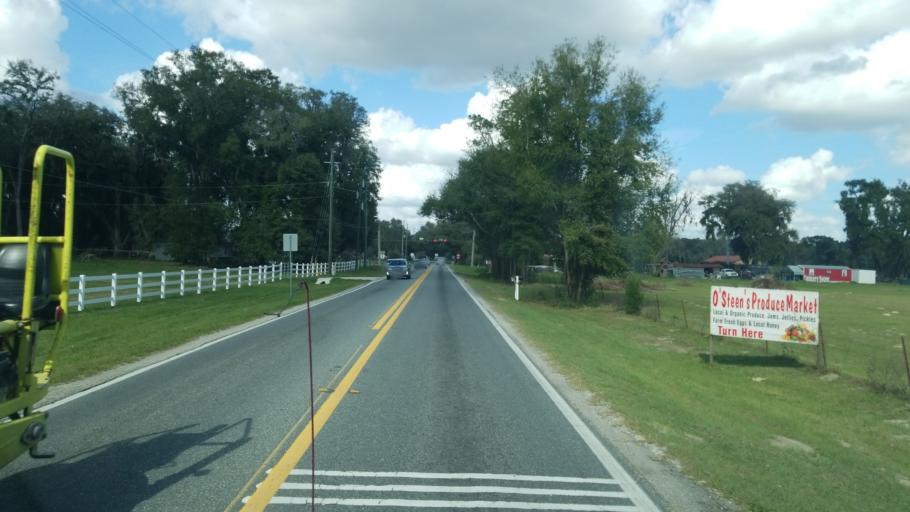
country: US
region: Florida
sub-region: Marion County
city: Belleview
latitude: 29.0095
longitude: -82.1199
